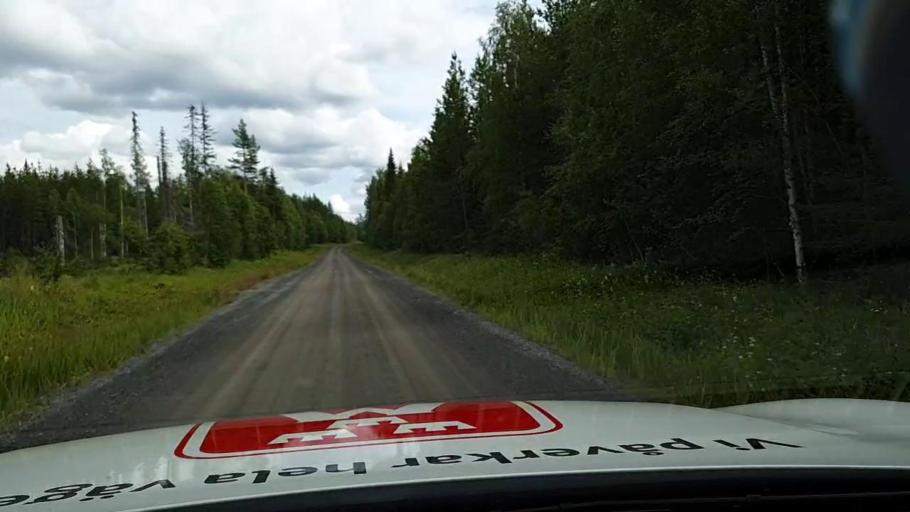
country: SE
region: Jaemtland
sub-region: OEstersunds Kommun
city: Lit
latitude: 63.3059
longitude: 15.2675
